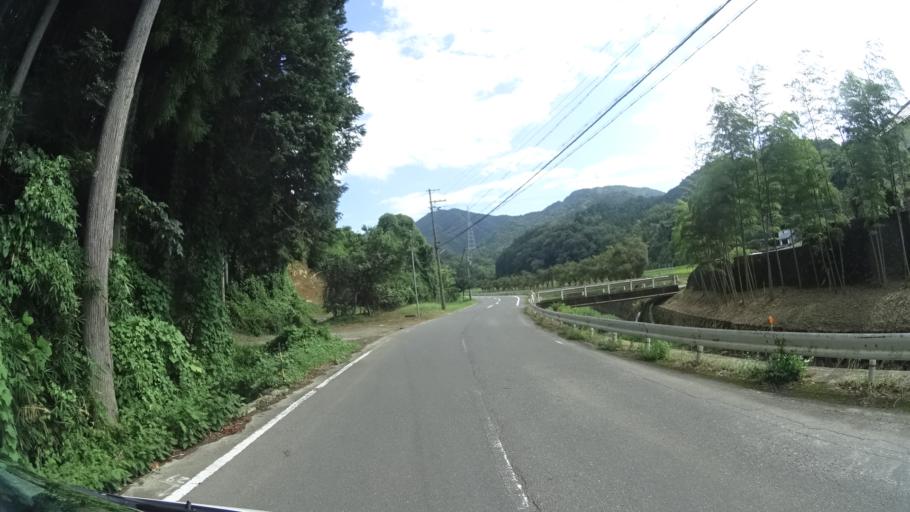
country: JP
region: Kyoto
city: Fukuchiyama
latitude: 35.3674
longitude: 135.1310
